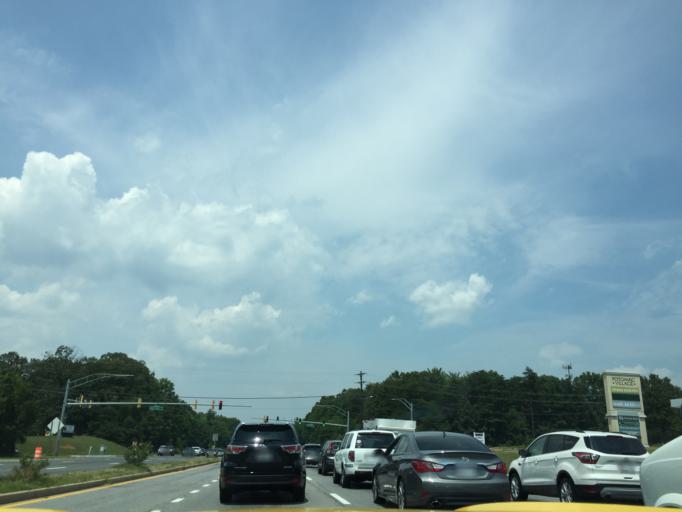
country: US
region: Maryland
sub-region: Prince George's County
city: Fort Washington
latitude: 38.7117
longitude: -76.9899
